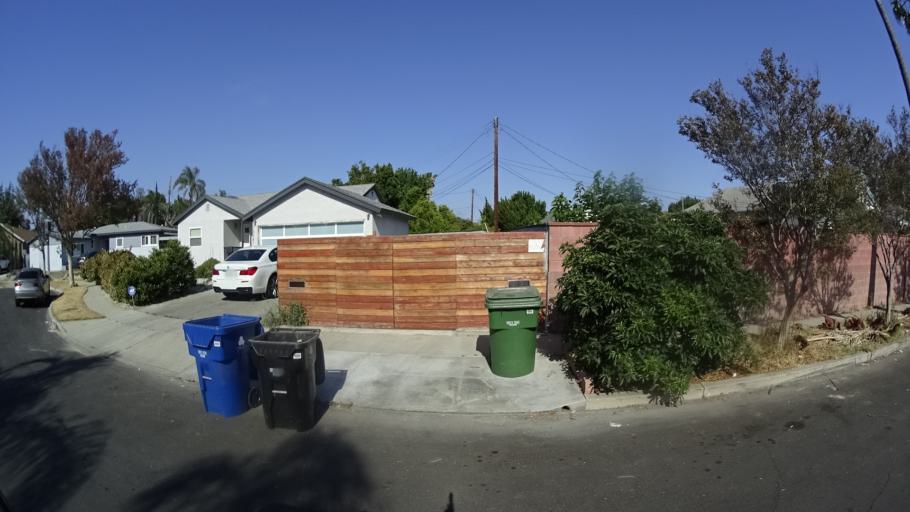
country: US
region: California
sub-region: Los Angeles County
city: Van Nuys
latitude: 34.2147
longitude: -118.4237
